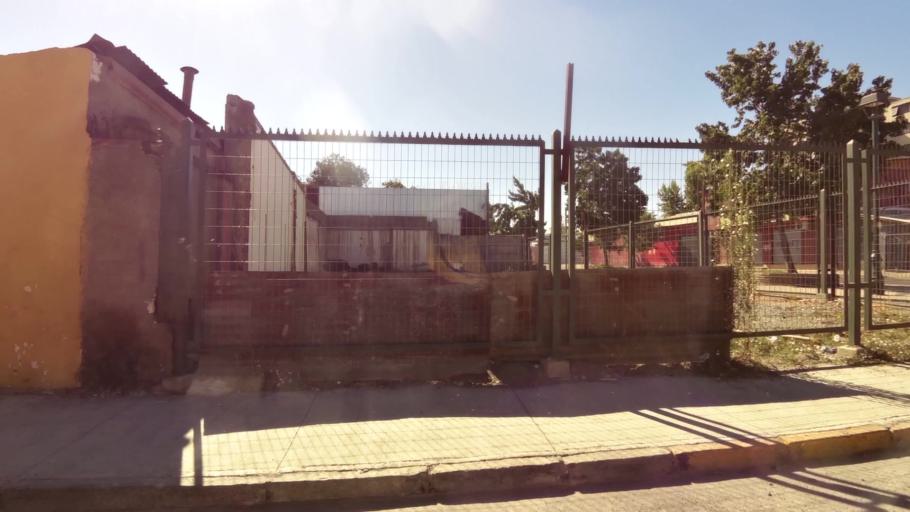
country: CL
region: O'Higgins
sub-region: Provincia de Cachapoal
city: Rancagua
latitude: -34.1670
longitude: -70.7478
